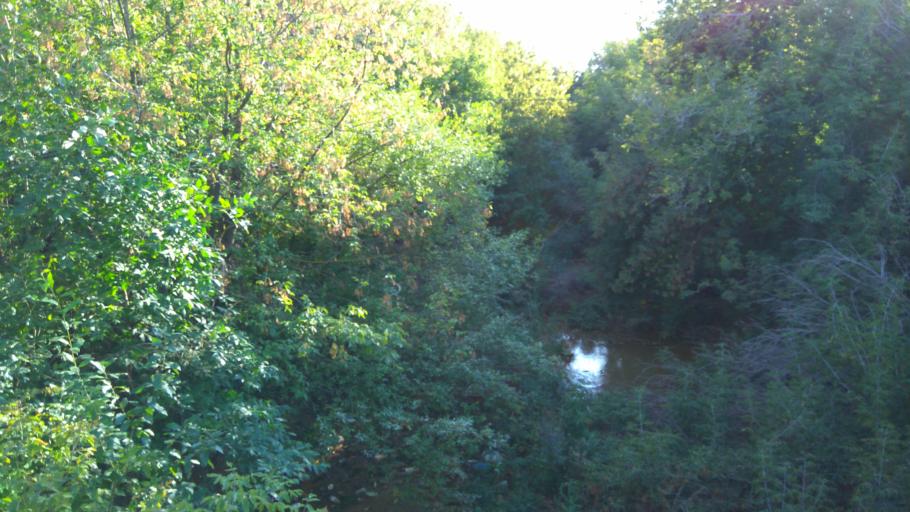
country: RU
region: Tatarstan
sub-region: Gorod Kazan'
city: Kazan
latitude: 55.7361
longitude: 49.0960
